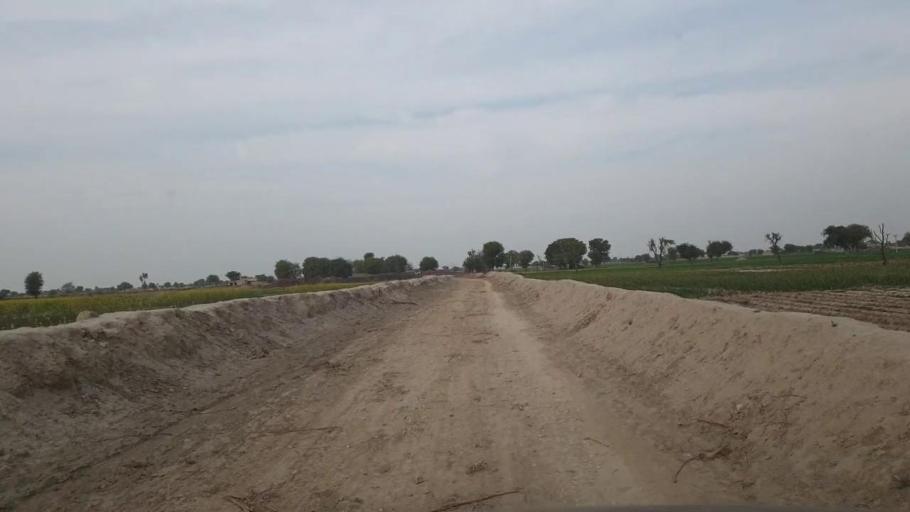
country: PK
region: Sindh
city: Shahpur Chakar
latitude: 26.1200
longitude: 68.5102
